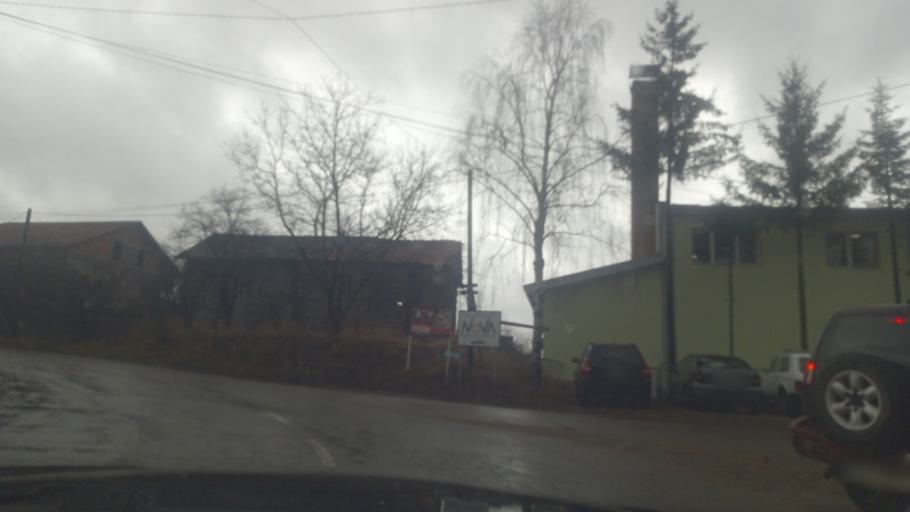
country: MK
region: Pehcevo
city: Pehcevo
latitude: 41.7602
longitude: 22.8805
